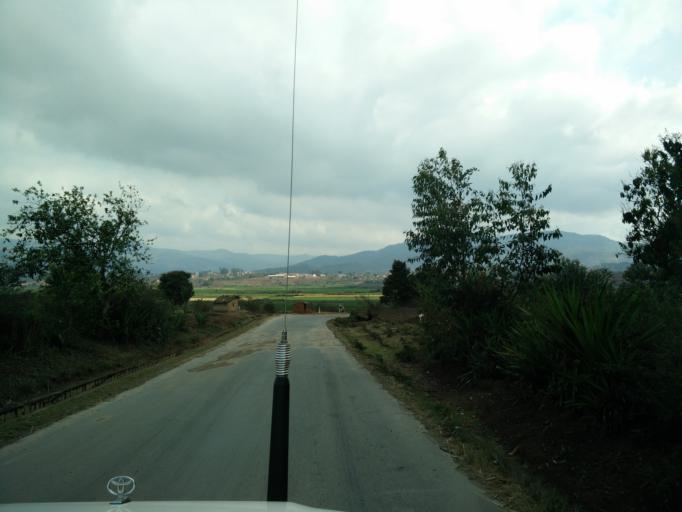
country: MG
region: Upper Matsiatra
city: Fianarantsoa
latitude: -21.3549
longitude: 47.1834
